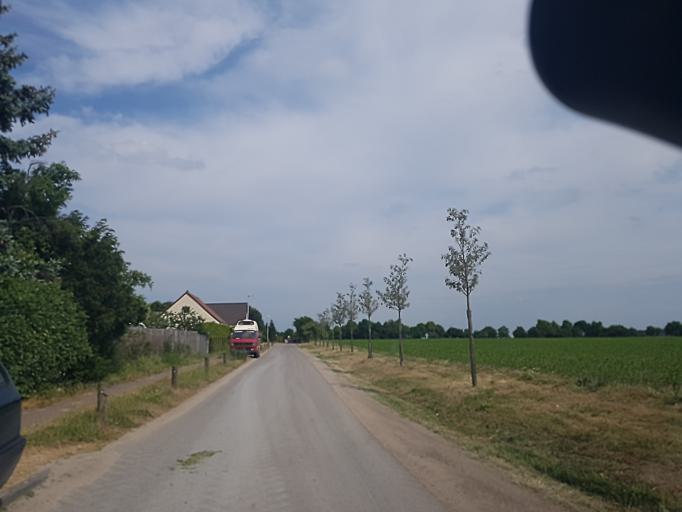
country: DE
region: Brandenburg
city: Gorzke
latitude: 52.1074
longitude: 12.3631
